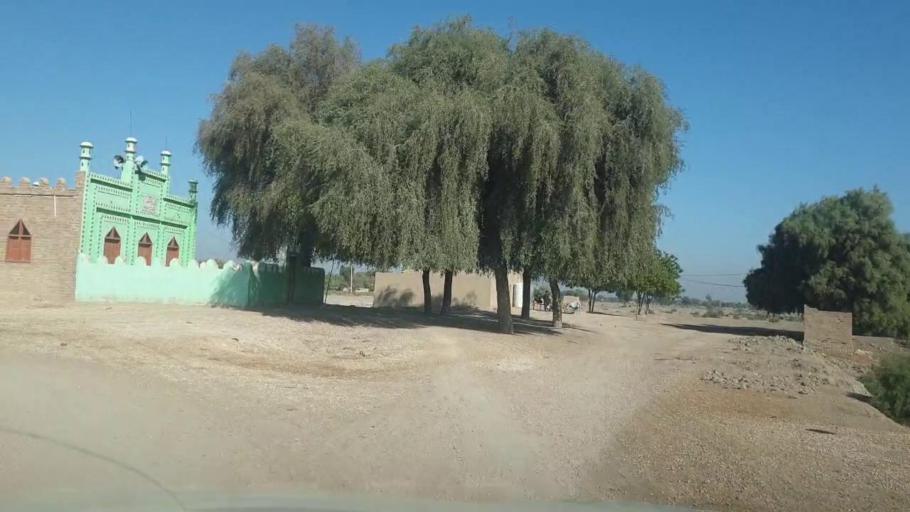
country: PK
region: Sindh
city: Bhan
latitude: 26.5481
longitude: 67.6560
